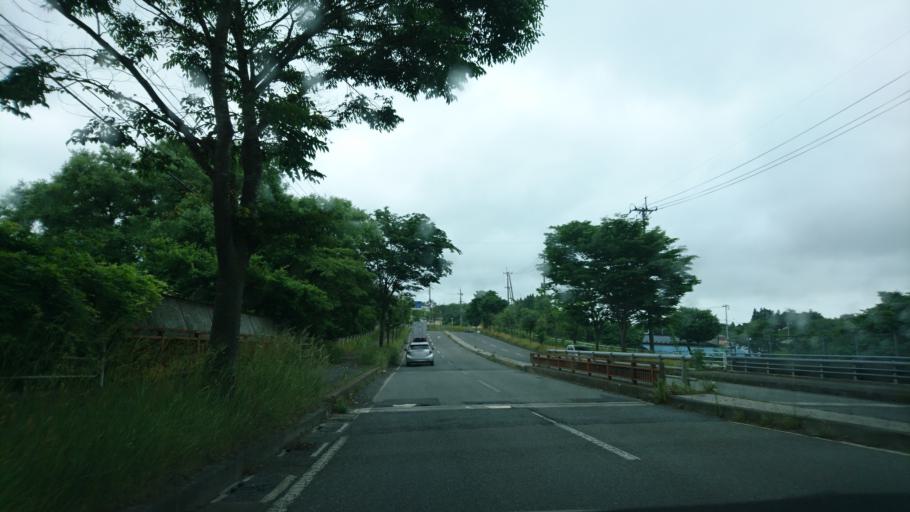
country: JP
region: Iwate
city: Ichinoseki
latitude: 38.9136
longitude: 141.1594
